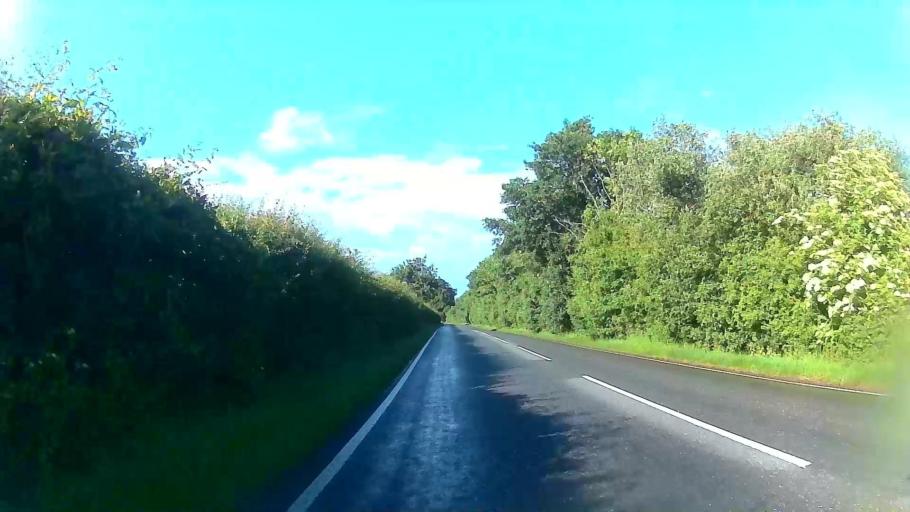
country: GB
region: England
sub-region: Essex
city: Writtle
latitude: 51.7175
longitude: 0.3977
